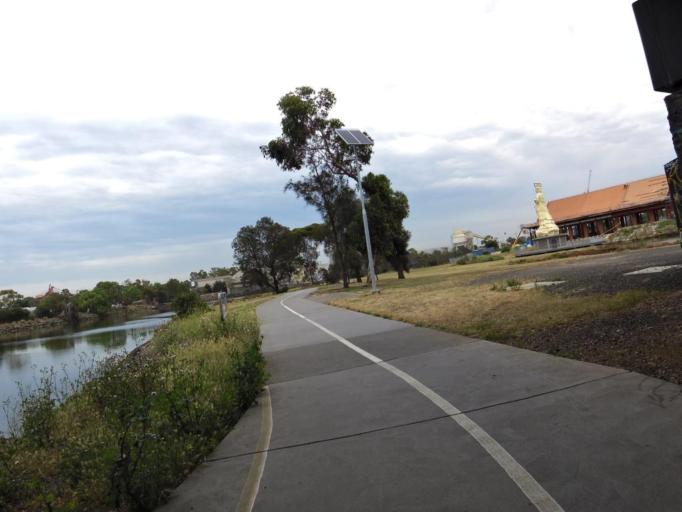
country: AU
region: Victoria
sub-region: Melbourne
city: Ascot Vale
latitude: -37.7983
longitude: 144.9162
